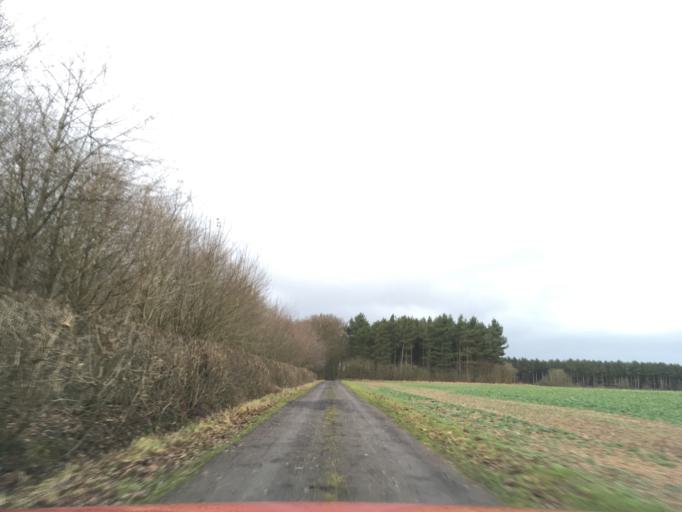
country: GB
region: England
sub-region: Nottinghamshire
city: East Leake
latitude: 52.8445
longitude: -1.1966
